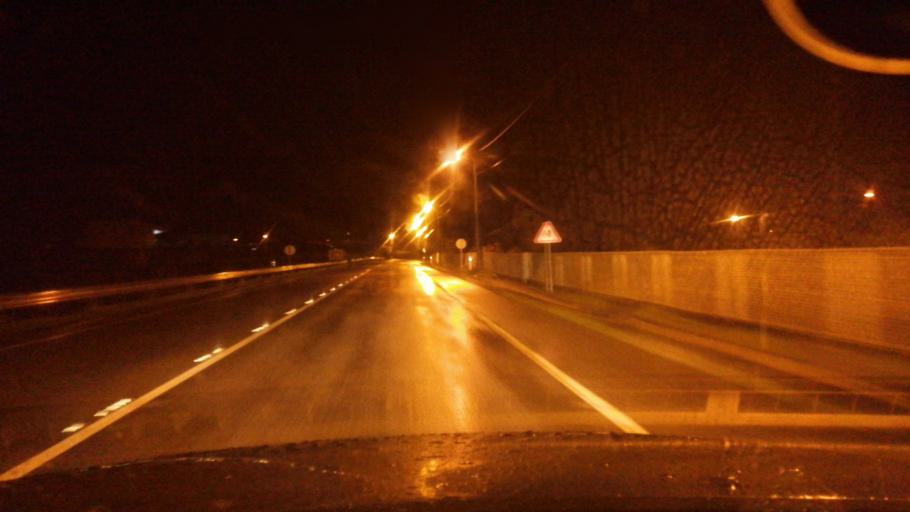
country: PT
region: Viseu
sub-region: Sernancelhe
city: Sernancelhe
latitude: 40.9116
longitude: -7.4567
